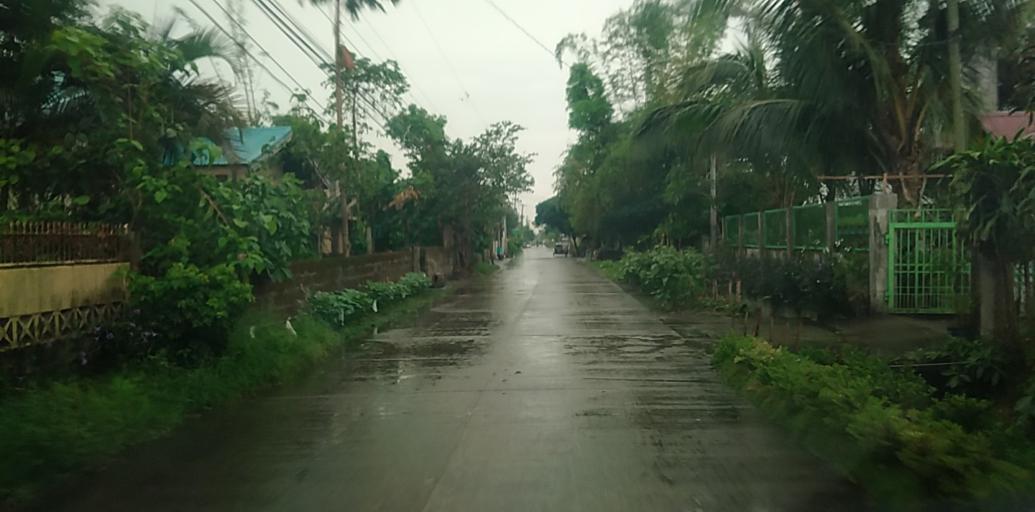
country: PH
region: Central Luzon
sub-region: Province of Pampanga
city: Arenas
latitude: 15.1657
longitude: 120.6890
